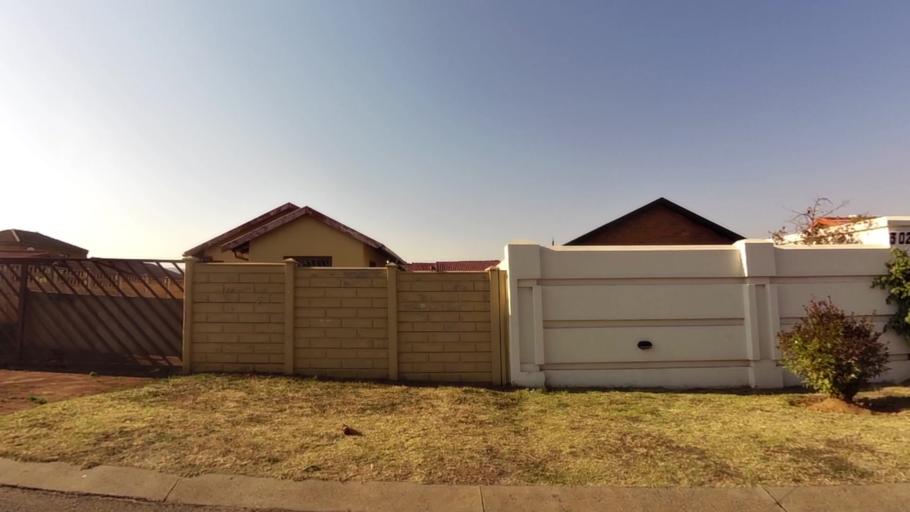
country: ZA
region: Gauteng
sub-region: City of Johannesburg Metropolitan Municipality
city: Soweto
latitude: -26.2918
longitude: 27.9489
